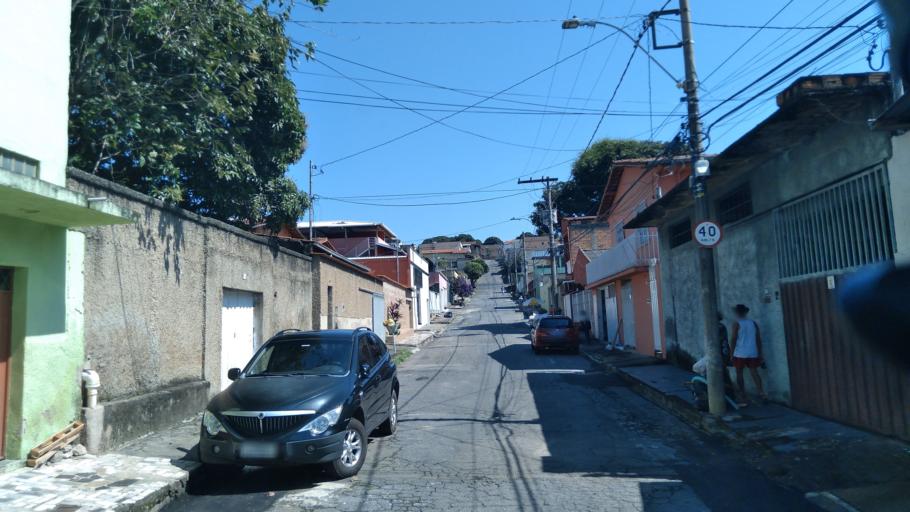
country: BR
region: Minas Gerais
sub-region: Contagem
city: Contagem
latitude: -19.9022
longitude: -44.0216
